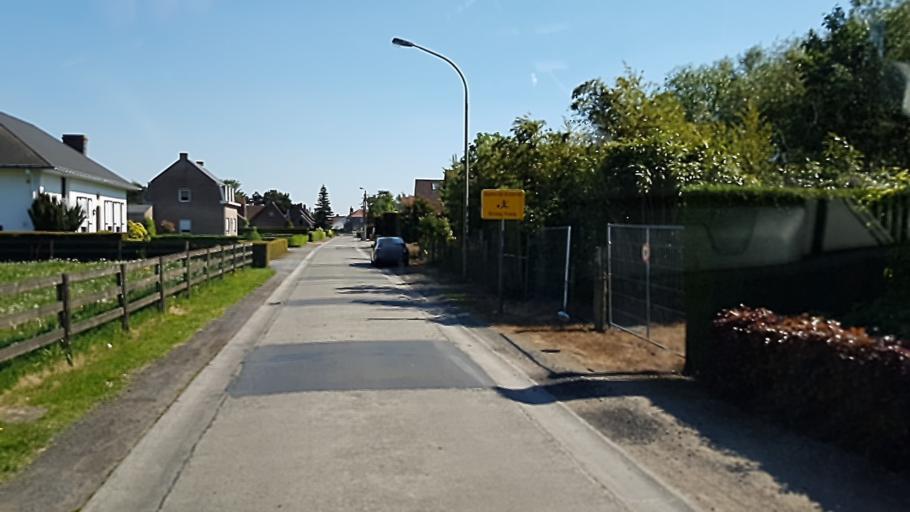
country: BE
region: Flanders
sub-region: Provincie Oost-Vlaanderen
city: Lochristi
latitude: 51.0873
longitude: 3.8072
